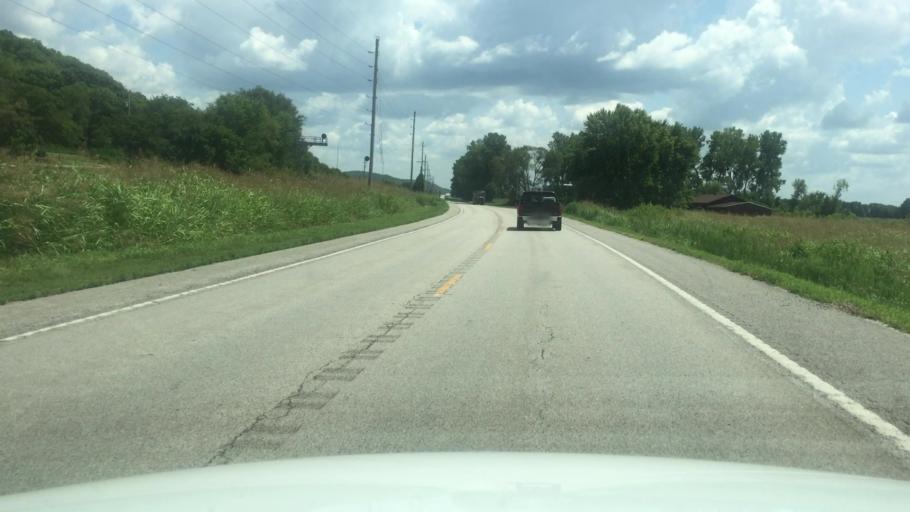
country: US
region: Kansas
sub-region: Atchison County
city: Atchison
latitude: 39.5325
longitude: -95.0371
